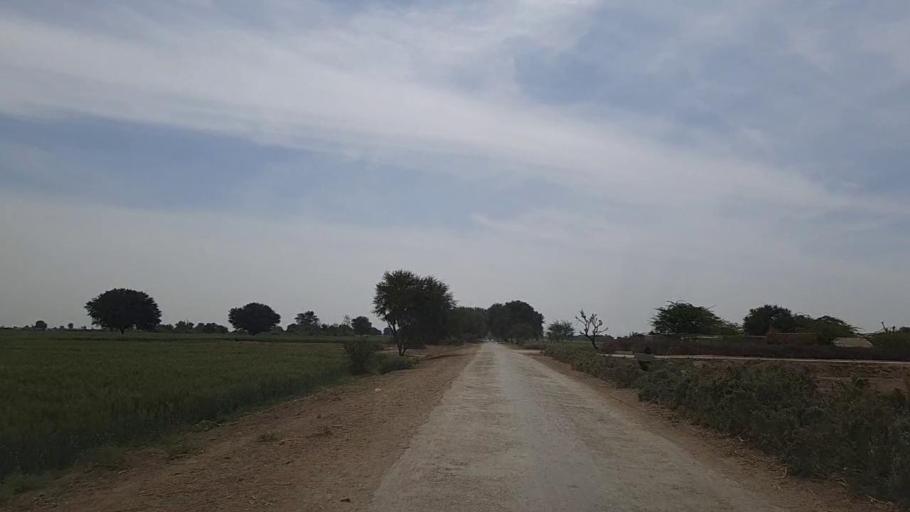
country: PK
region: Sindh
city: Samaro
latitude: 25.2885
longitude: 69.4538
